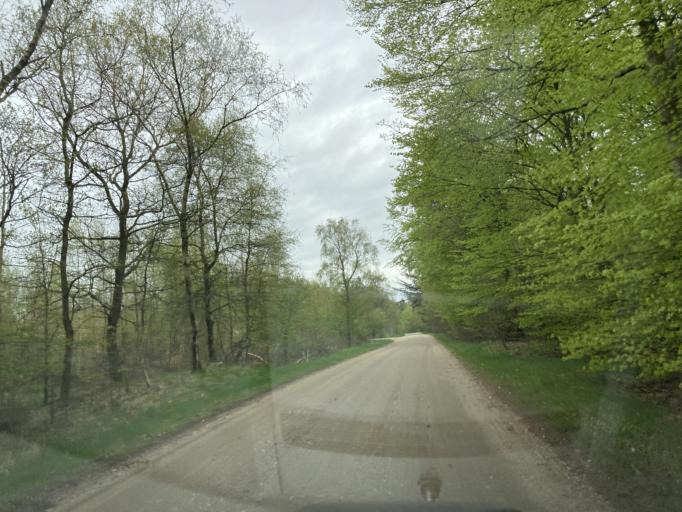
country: DK
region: North Denmark
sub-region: Thisted Kommune
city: Hanstholm
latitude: 57.0254
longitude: 8.5932
